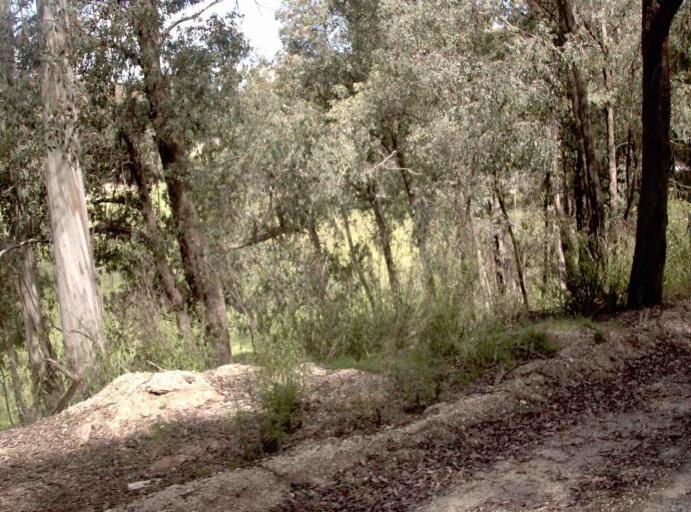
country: AU
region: New South Wales
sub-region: Bombala
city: Bombala
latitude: -37.1826
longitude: 148.7154
